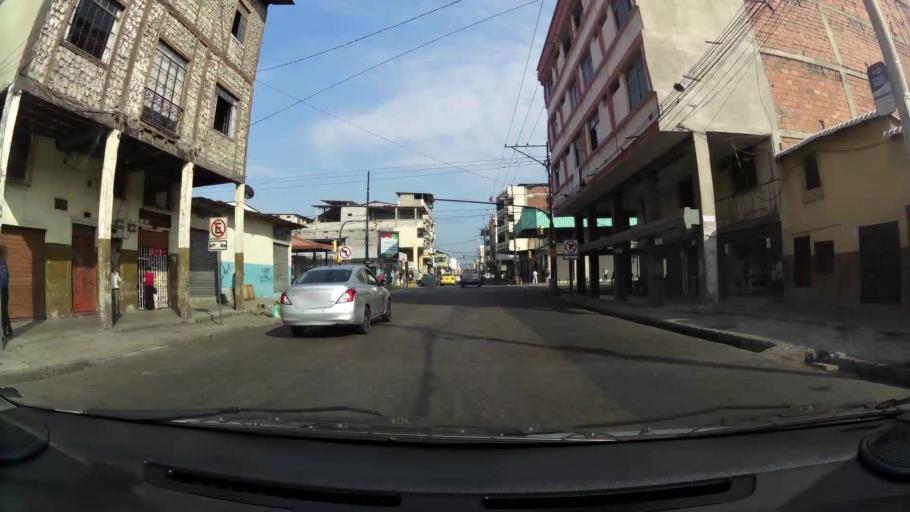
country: EC
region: Guayas
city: Guayaquil
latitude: -2.1953
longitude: -79.8898
